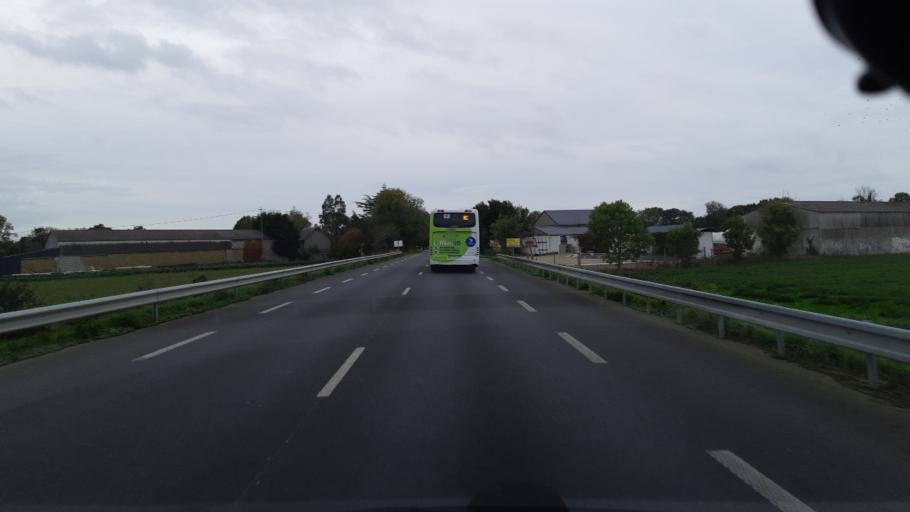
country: FR
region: Lower Normandy
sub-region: Departement de la Manche
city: Brehal
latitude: 48.8764
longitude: -1.5339
